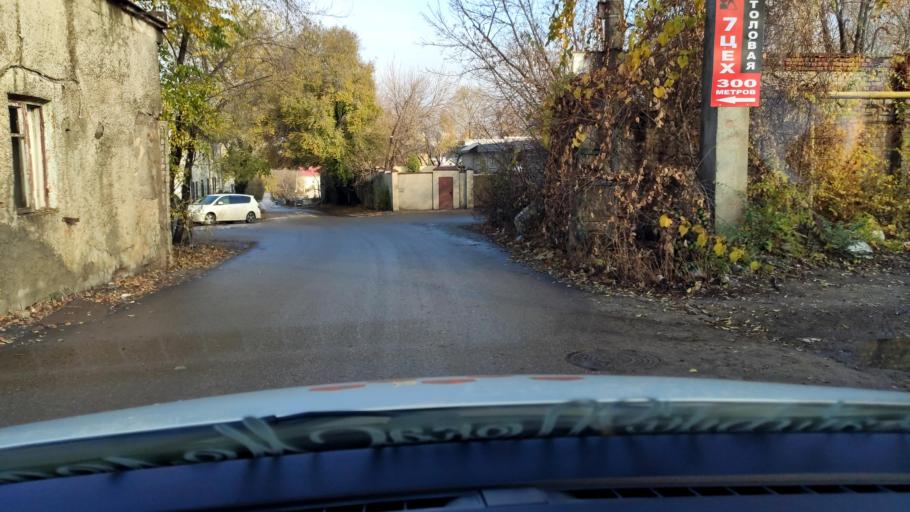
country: RU
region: Voronezj
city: Voronezh
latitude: 51.6906
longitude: 39.1754
